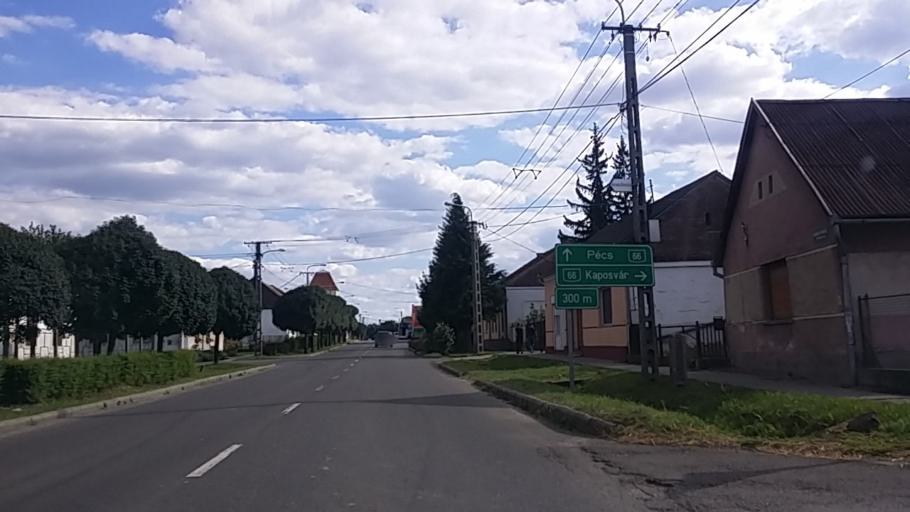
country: HU
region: Baranya
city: Sasd
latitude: 46.2573
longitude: 18.1056
